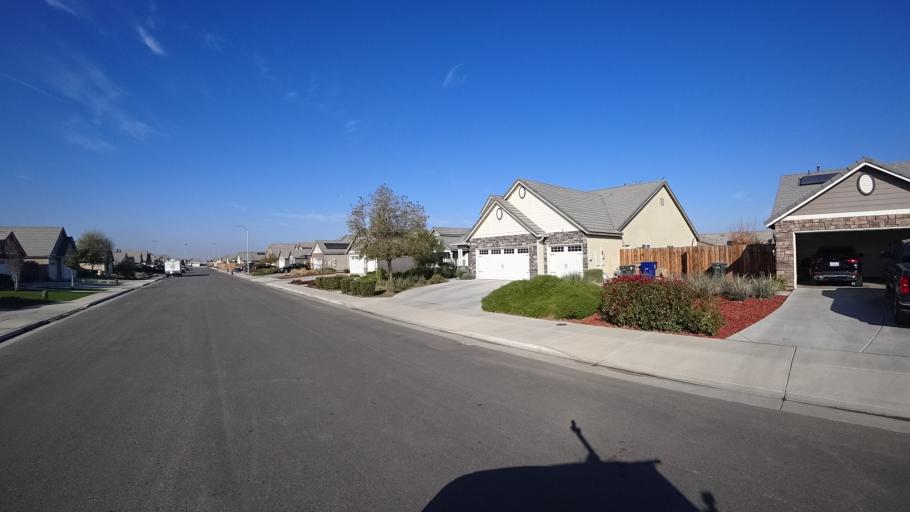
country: US
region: California
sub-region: Kern County
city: Greenfield
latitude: 35.2721
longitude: -119.0709
